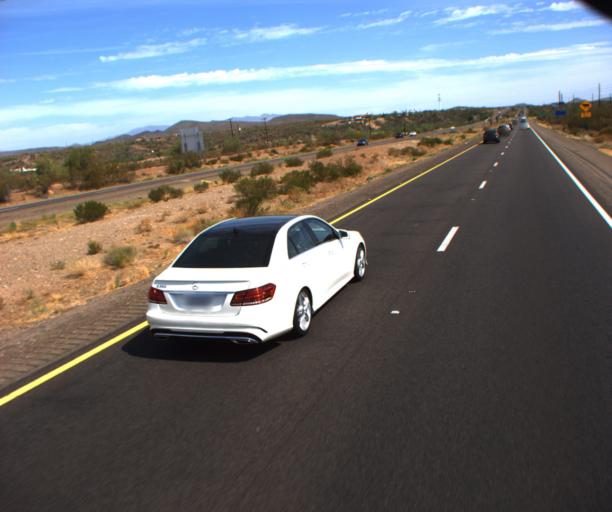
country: US
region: Arizona
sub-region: Maricopa County
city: New River
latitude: 33.8985
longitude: -112.1466
